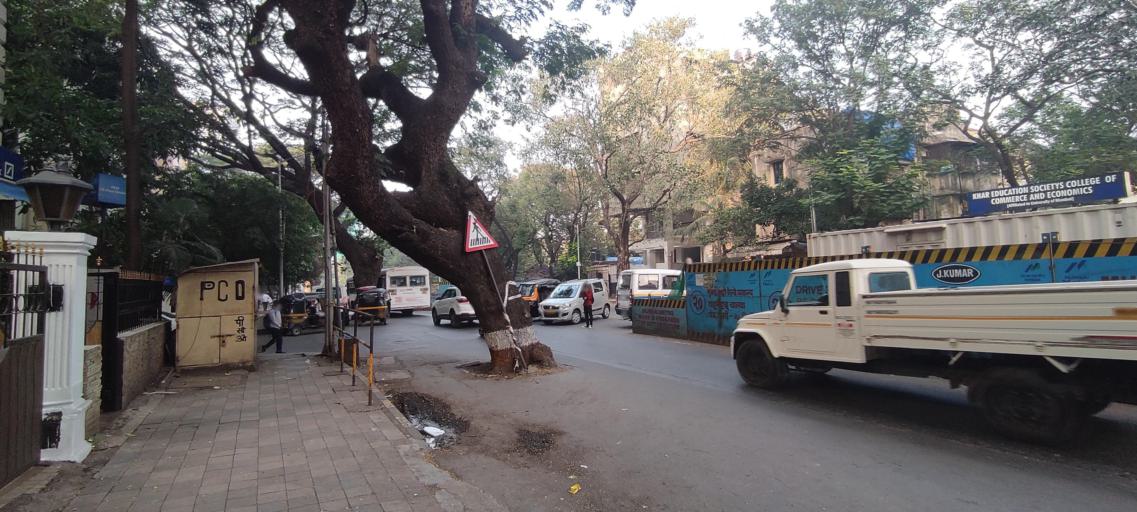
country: IN
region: Maharashtra
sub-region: Mumbai Suburban
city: Mumbai
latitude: 19.0723
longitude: 72.8374
